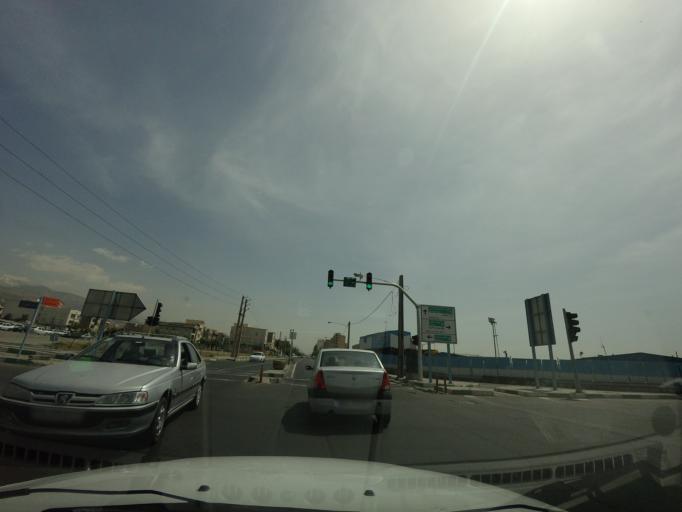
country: IR
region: Tehran
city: Shahr-e Qods
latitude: 35.7450
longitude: 51.2418
